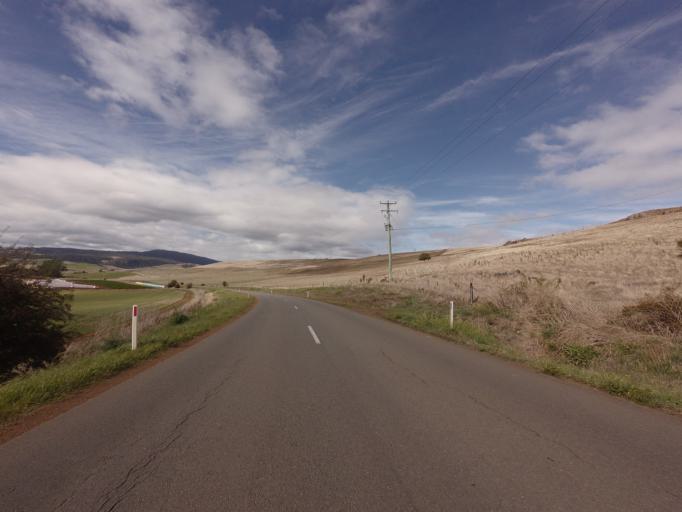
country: AU
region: Tasmania
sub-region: Derwent Valley
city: New Norfolk
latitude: -42.6978
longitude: 146.9286
